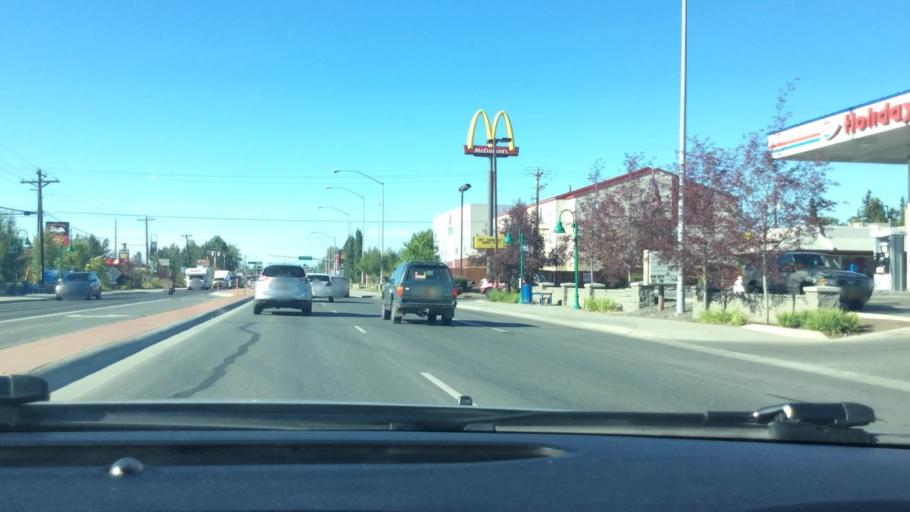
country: US
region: Alaska
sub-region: Anchorage Municipality
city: Elmendorf Air Force Base
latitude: 61.2207
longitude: -149.7334
